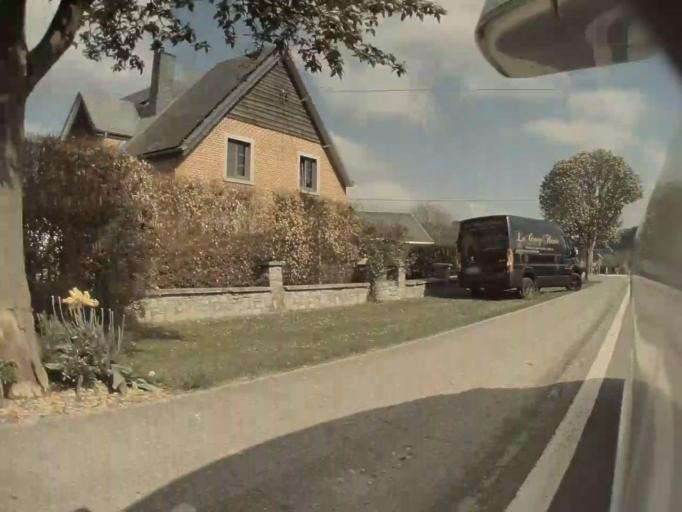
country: BE
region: Wallonia
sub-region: Province du Luxembourg
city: Tellin
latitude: 50.0847
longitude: 5.2226
